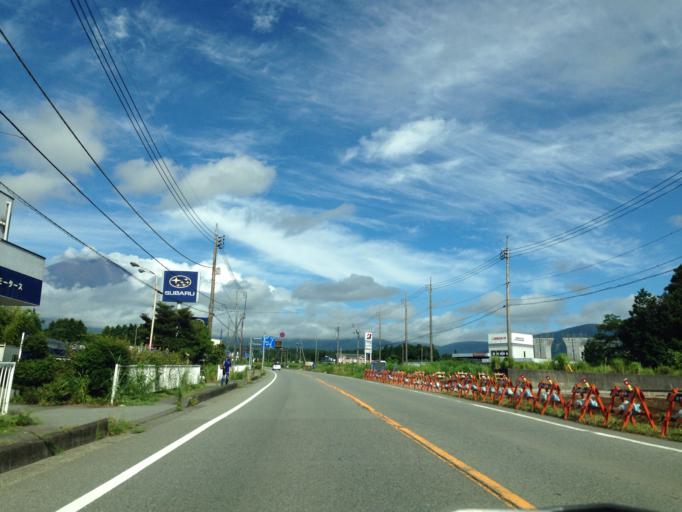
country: JP
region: Shizuoka
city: Gotemba
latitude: 35.3172
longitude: 138.9191
